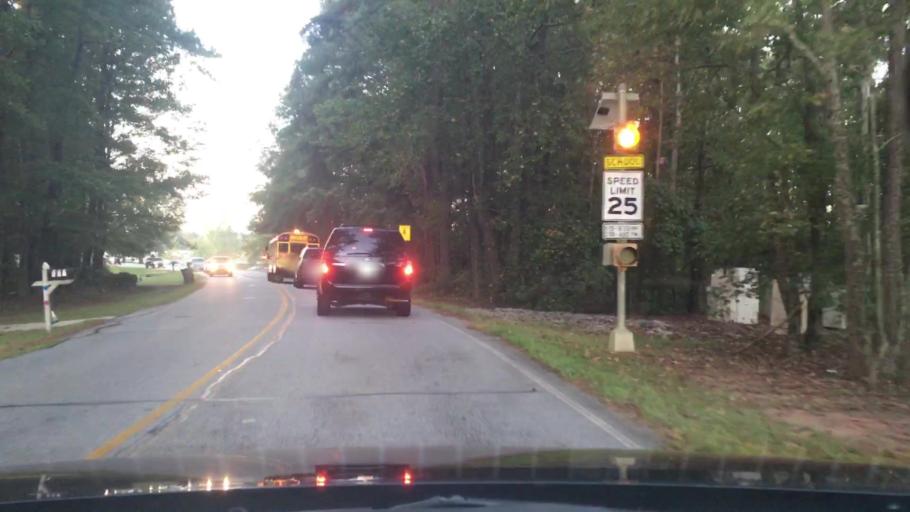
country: US
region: Georgia
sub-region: Coweta County
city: East Newnan
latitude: 33.3963
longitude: -84.6992
